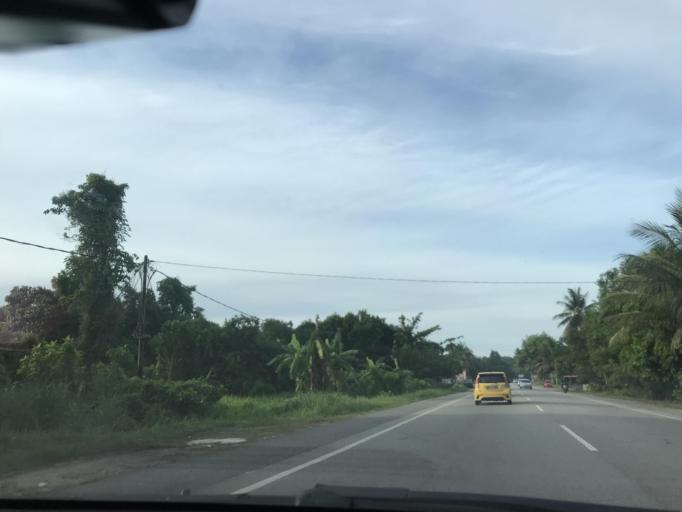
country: MY
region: Kelantan
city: Kampong Pangkal Kalong
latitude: 5.9659
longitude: 102.1936
